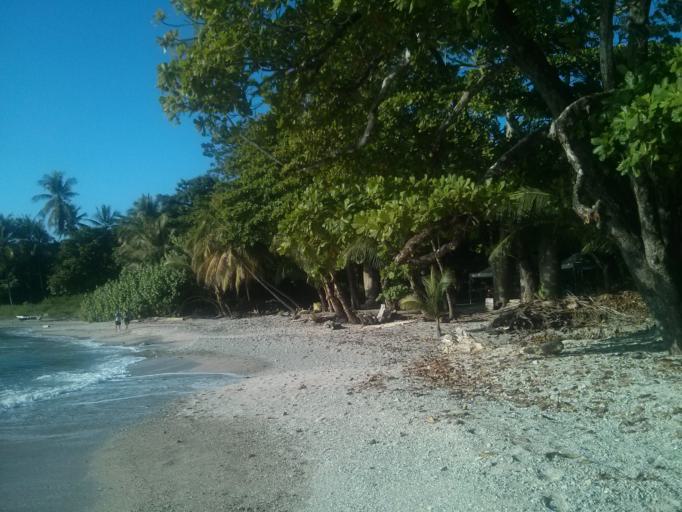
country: CR
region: Puntarenas
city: Paquera
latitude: 9.6158
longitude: -85.1442
